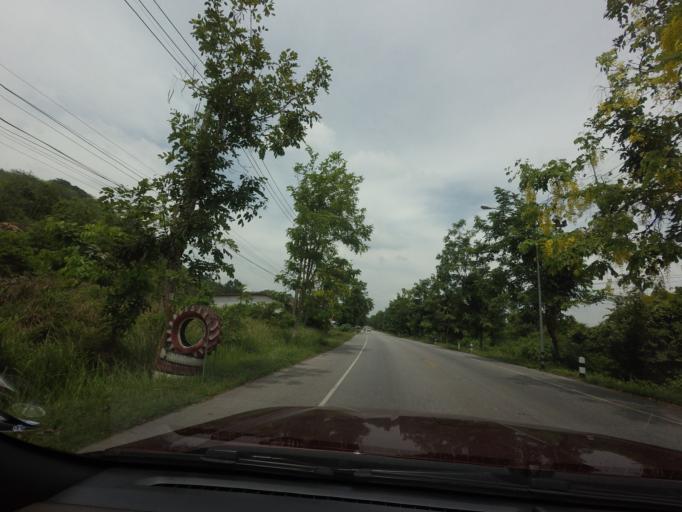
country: TH
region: Pattani
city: Mae Lan
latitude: 6.6332
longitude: 101.3020
